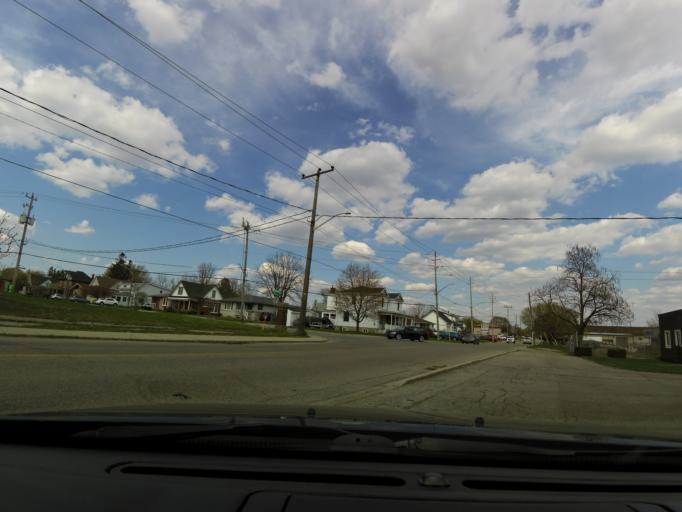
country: CA
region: Ontario
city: Cambridge
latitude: 43.3698
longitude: -80.3068
